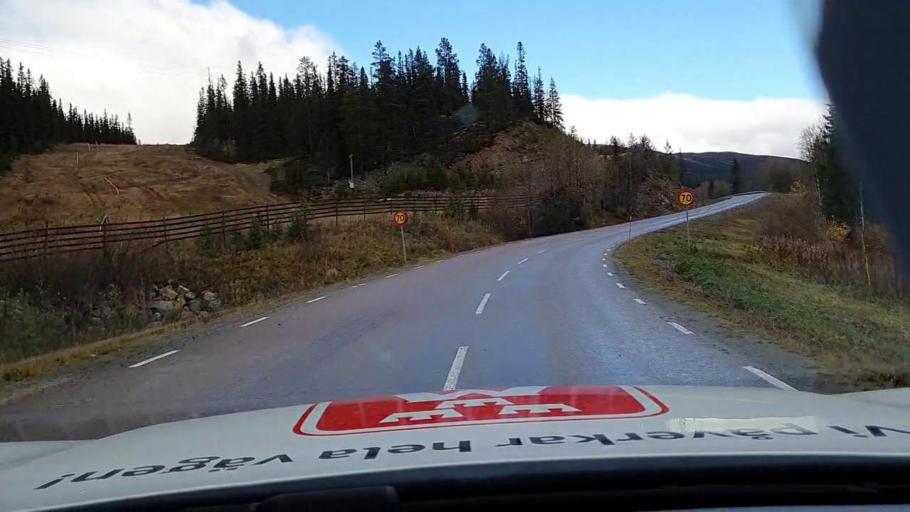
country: SE
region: Jaemtland
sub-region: Are Kommun
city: Jarpen
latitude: 63.0872
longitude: 13.7713
